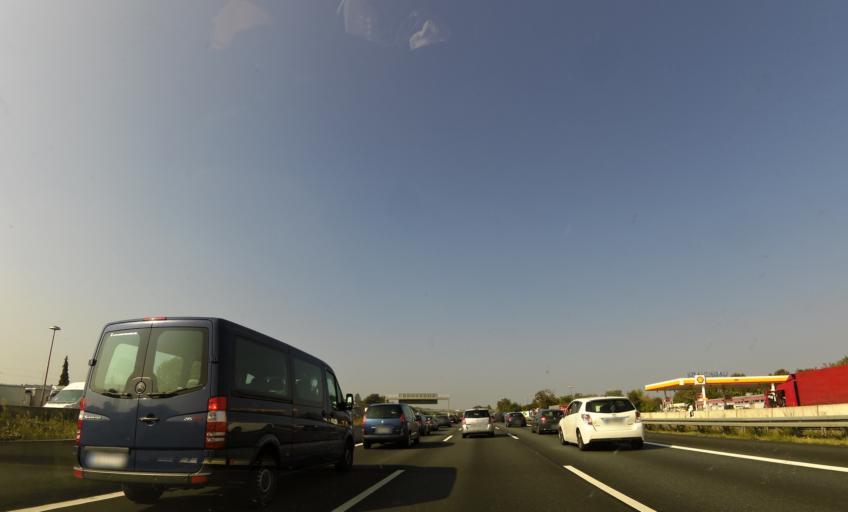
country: DE
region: Baden-Wuerttemberg
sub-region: Karlsruhe Region
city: Sinsheim
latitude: 49.2428
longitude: 8.8823
